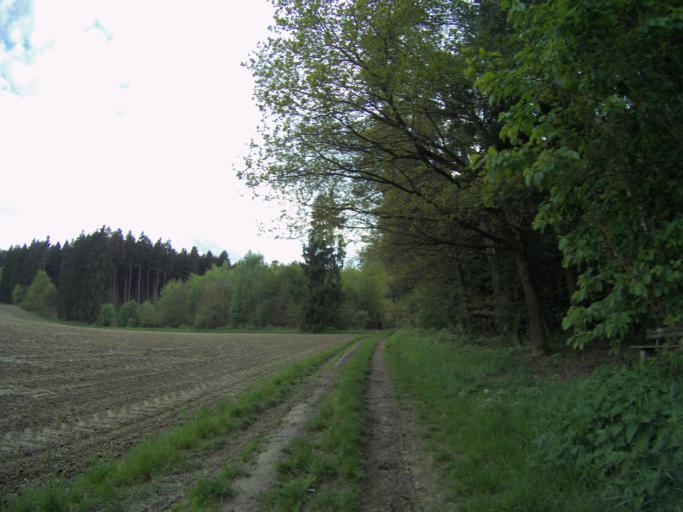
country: DE
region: Bavaria
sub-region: Upper Bavaria
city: Freising
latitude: 48.4203
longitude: 11.7627
